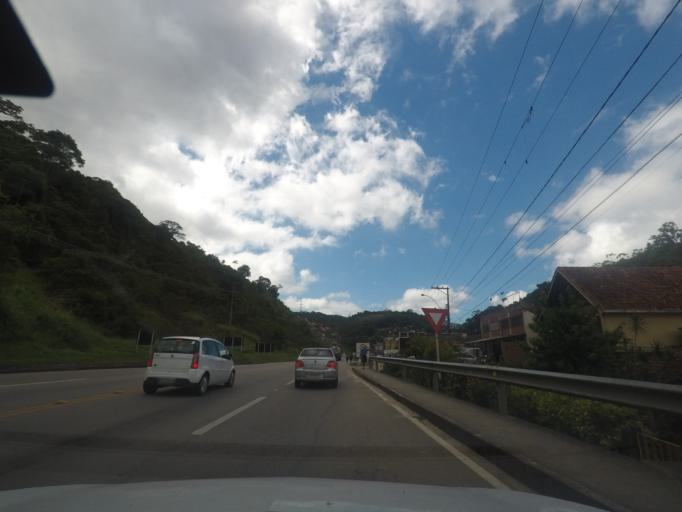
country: BR
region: Rio de Janeiro
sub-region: Teresopolis
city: Teresopolis
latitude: -22.3911
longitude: -42.9533
